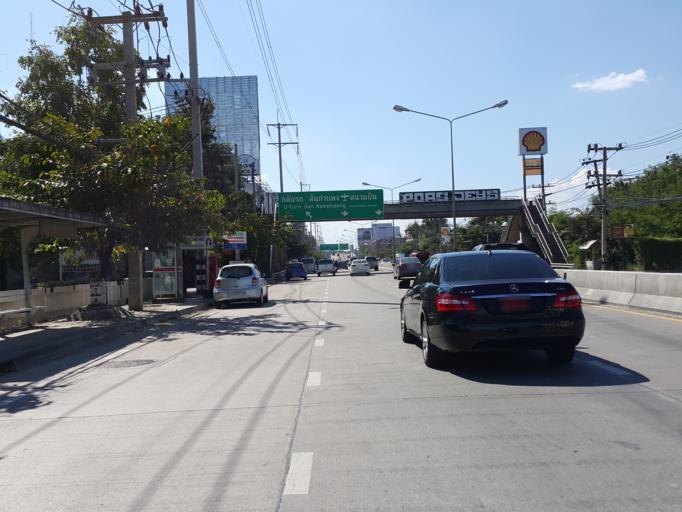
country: TH
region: Chiang Mai
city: Chiang Mai
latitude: 18.7630
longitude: 99.0250
